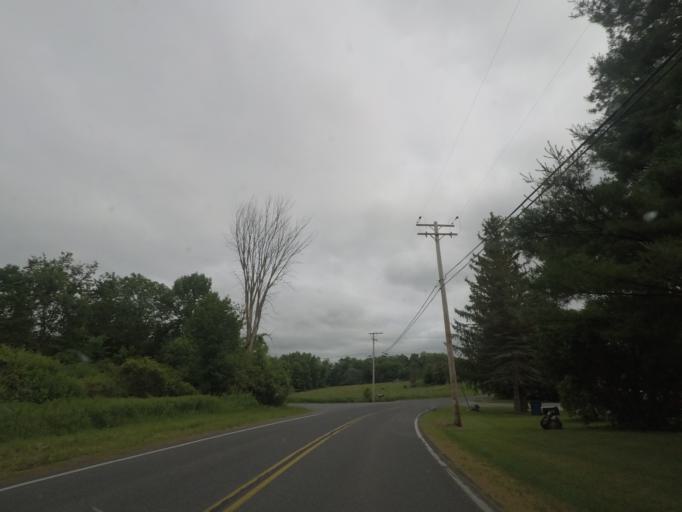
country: US
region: New York
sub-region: Dutchess County
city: Pine Plains
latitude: 41.9680
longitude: -73.5008
